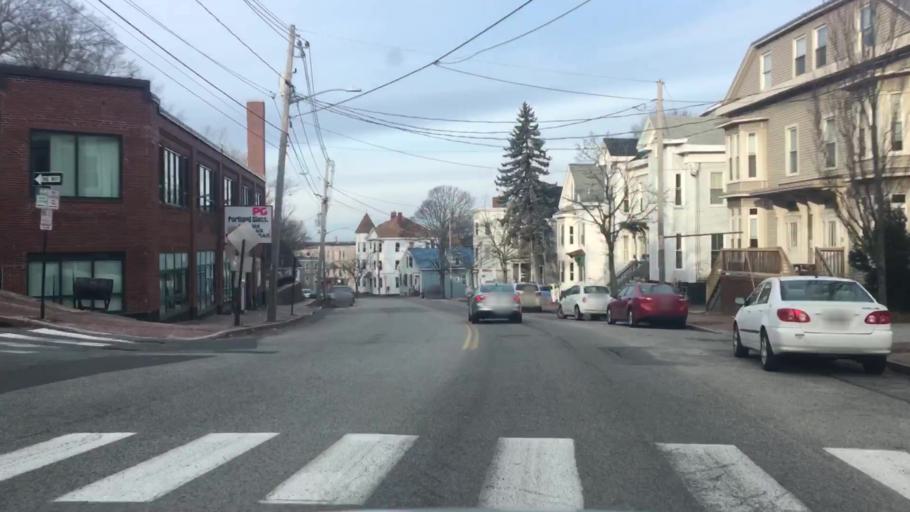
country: US
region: Maine
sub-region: Cumberland County
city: Portland
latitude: 43.6545
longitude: -70.2736
